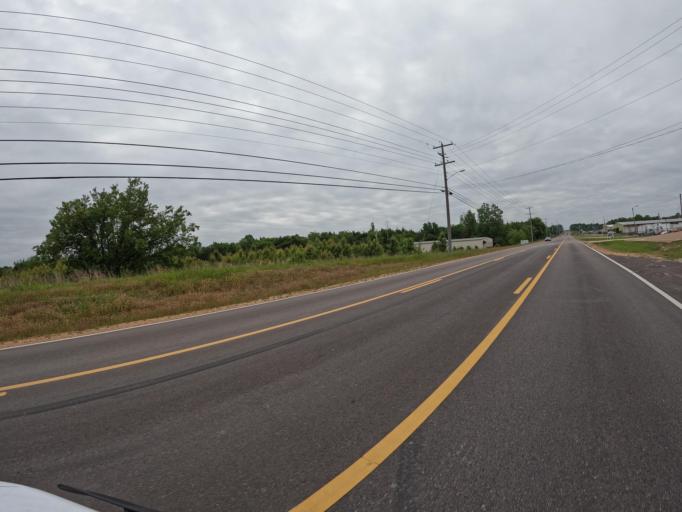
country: US
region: Mississippi
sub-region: Lee County
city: Tupelo
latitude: 34.2782
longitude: -88.7643
